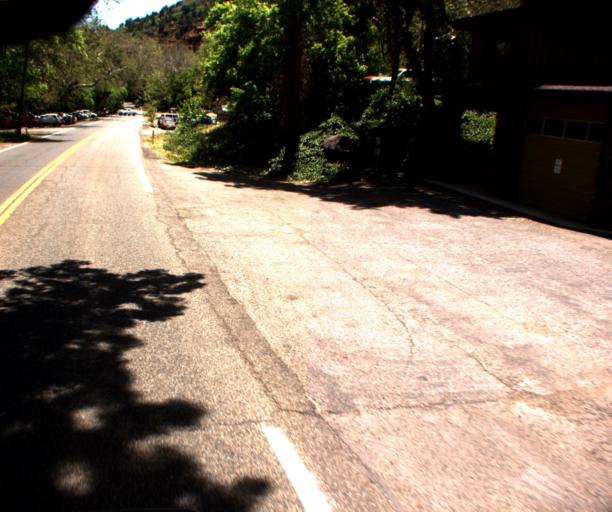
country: US
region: Arizona
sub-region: Coconino County
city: Sedona
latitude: 34.9112
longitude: -111.7282
